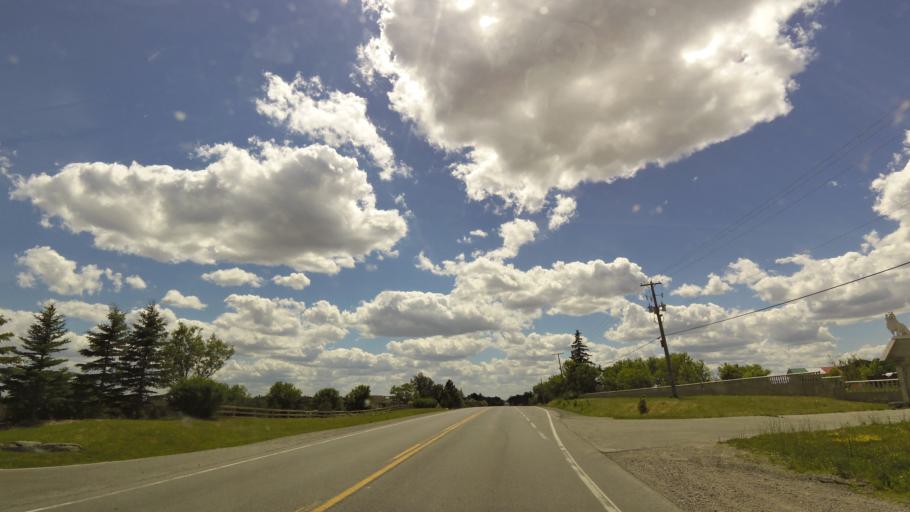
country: CA
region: Ontario
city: Uxbridge
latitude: 44.0404
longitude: -79.1903
